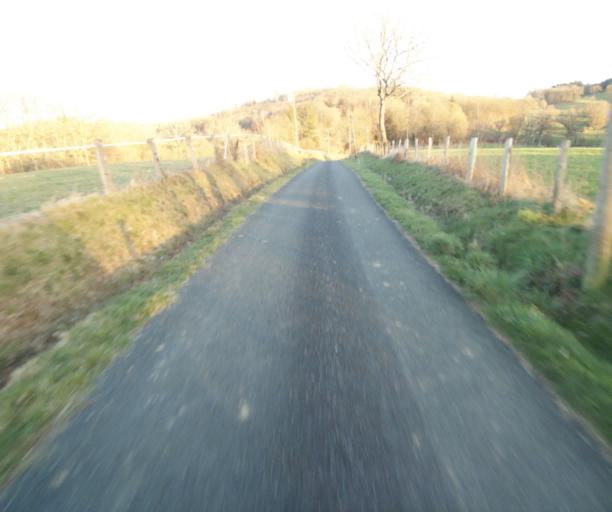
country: FR
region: Limousin
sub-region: Departement de la Correze
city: Uzerche
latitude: 45.3639
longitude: 1.6115
